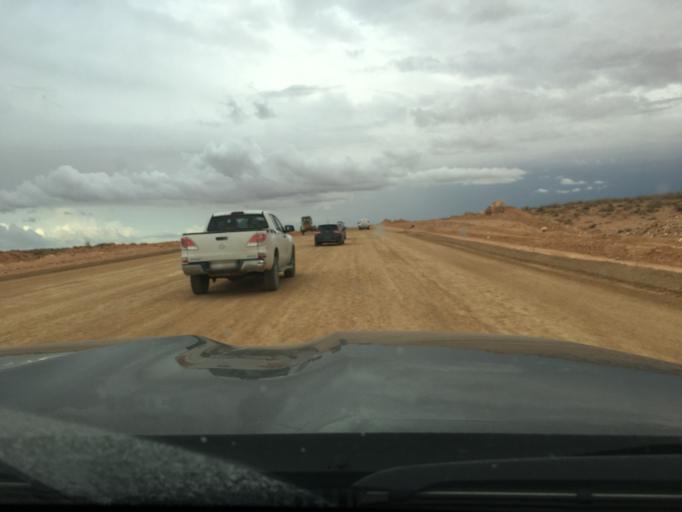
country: TN
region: Madanin
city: Medenine
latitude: 33.2630
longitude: 10.5794
